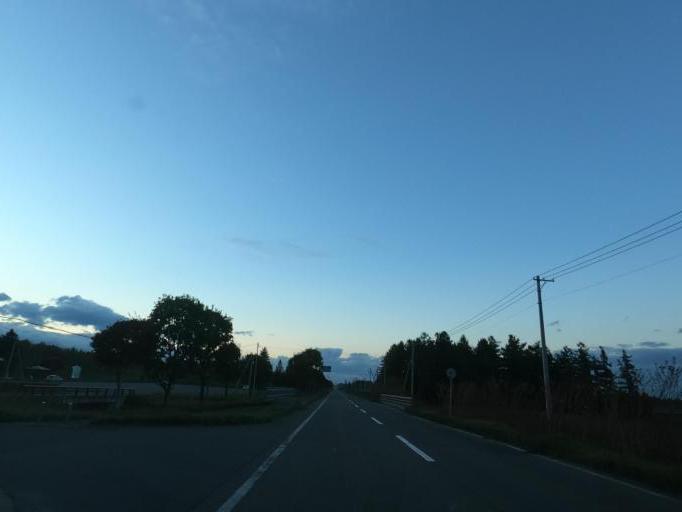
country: JP
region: Hokkaido
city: Obihiro
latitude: 42.6396
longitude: 143.2048
